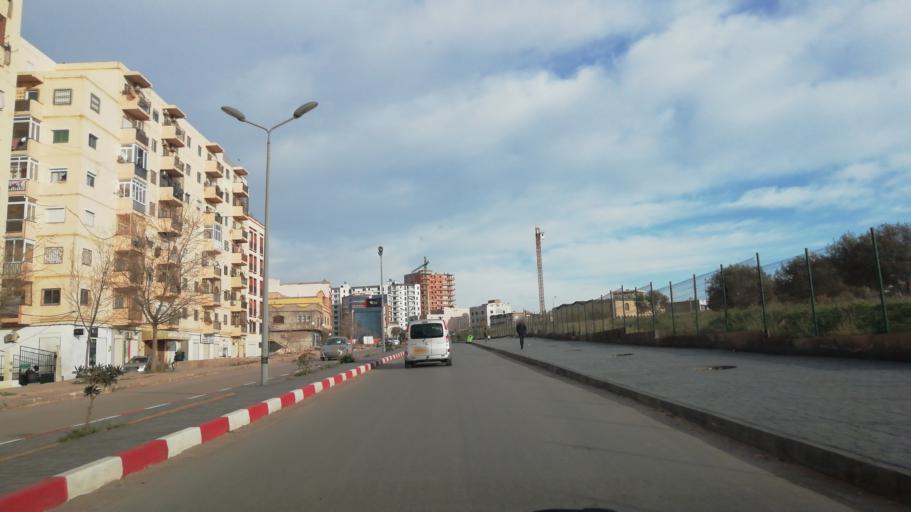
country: DZ
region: Oran
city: Bir el Djir
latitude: 35.7204
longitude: -0.5871
